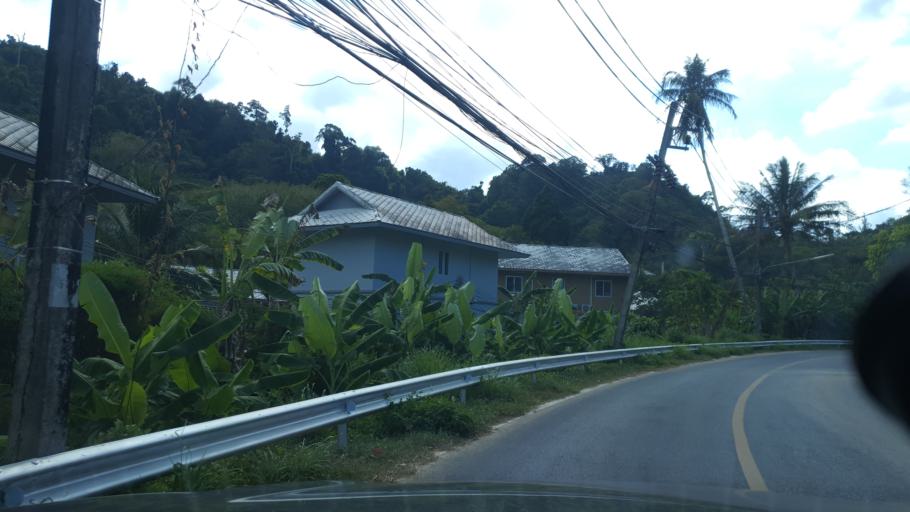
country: TH
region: Phuket
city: Thalang
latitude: 8.0659
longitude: 98.2914
